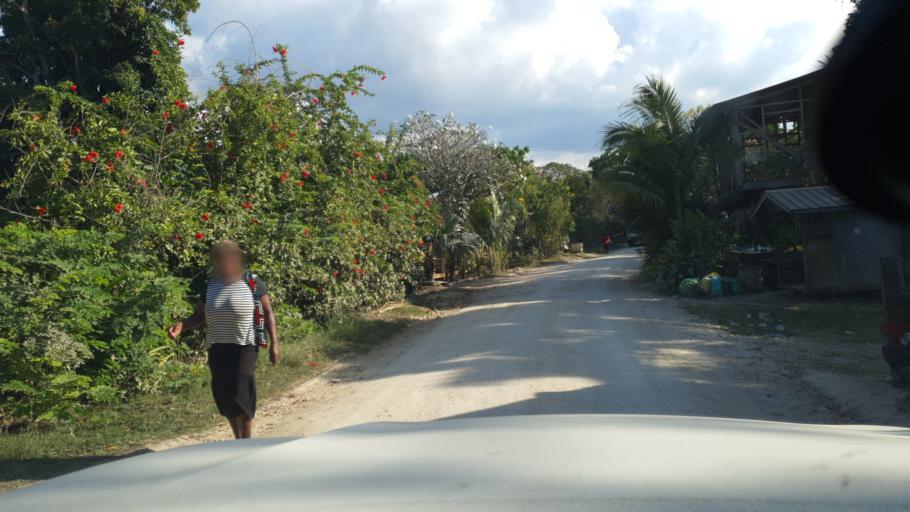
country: SB
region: Guadalcanal
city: Honiara
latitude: -9.4521
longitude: 159.9932
